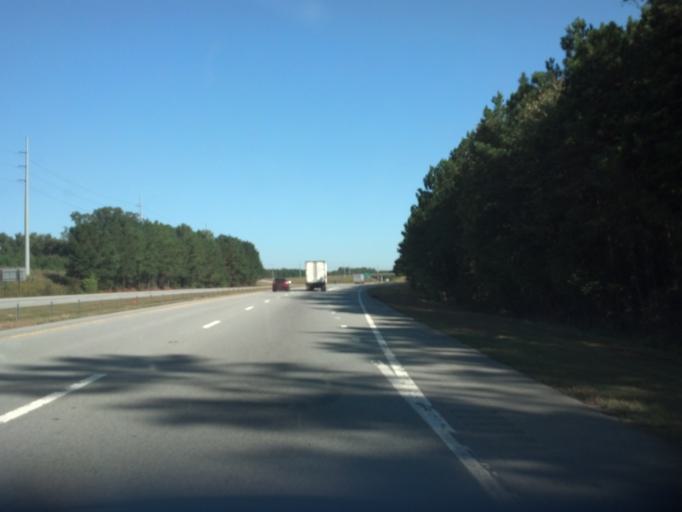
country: US
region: North Carolina
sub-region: Pitt County
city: Summerfield
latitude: 35.6237
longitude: -77.4361
